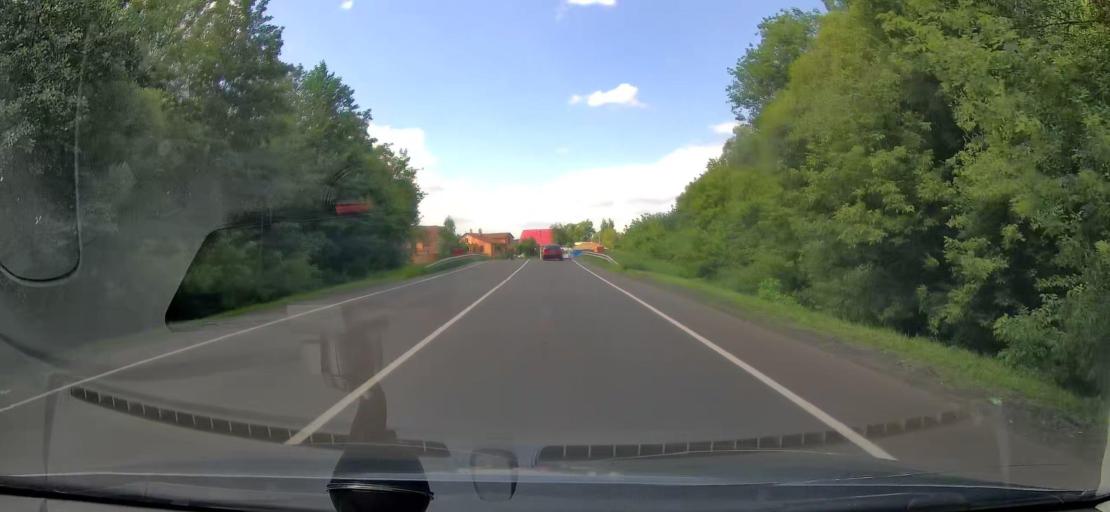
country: RU
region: Kursk
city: Zolotukhino
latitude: 51.9246
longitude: 36.3060
